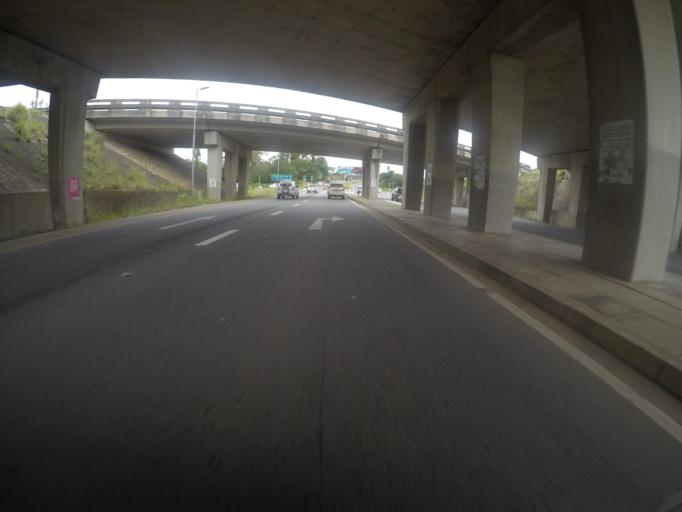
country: ZA
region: Eastern Cape
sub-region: Buffalo City Metropolitan Municipality
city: East London
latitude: -32.9636
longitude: 27.9198
